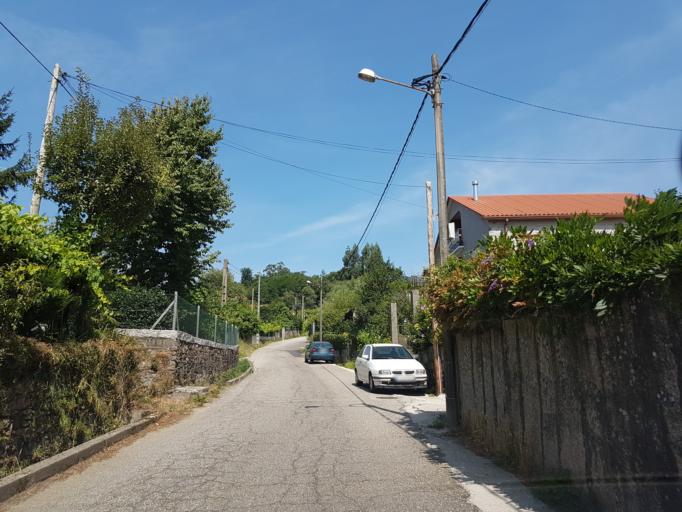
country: ES
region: Galicia
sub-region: Provincia de Pontevedra
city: Porrino
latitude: 42.2218
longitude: -8.6212
